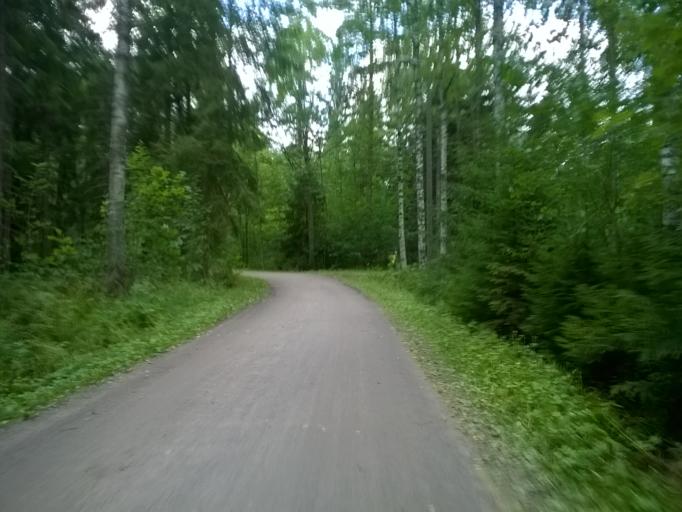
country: FI
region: Uusimaa
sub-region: Helsinki
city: Helsinki
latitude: 60.2588
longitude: 24.9123
